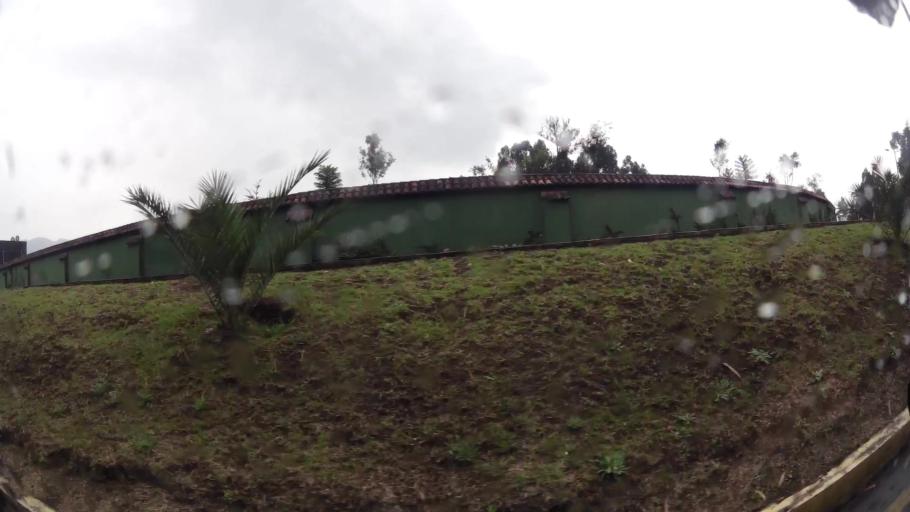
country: EC
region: Pichincha
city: Sangolqui
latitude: -0.3225
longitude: -78.4490
